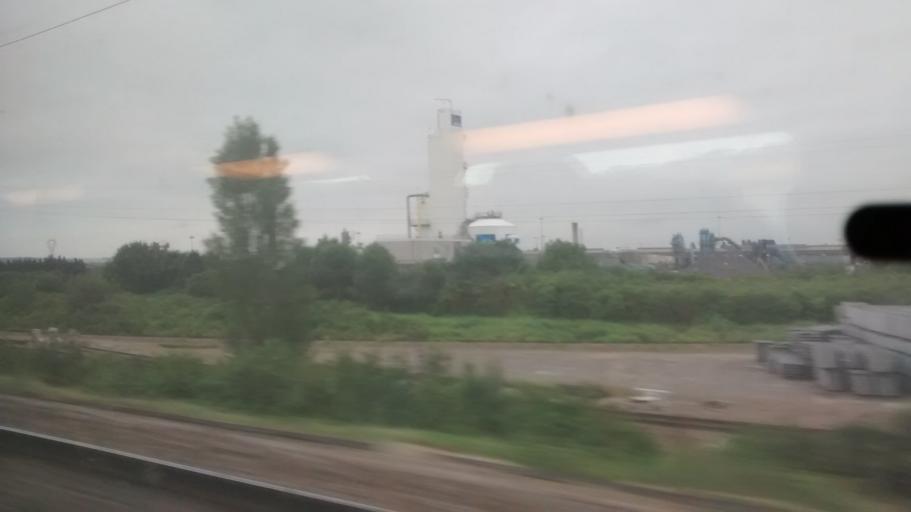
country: FR
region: Ile-de-France
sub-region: Departement de Seine-et-Marne
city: Saint-Germain-Laval
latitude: 48.3927
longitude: 2.9833
